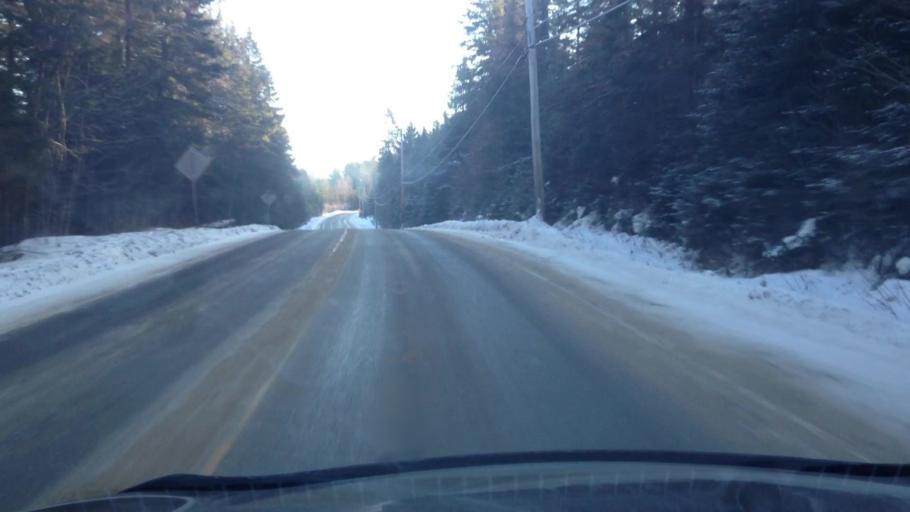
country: CA
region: Quebec
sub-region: Laurentides
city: Sainte-Agathe-des-Monts
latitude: 45.9207
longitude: -74.3865
